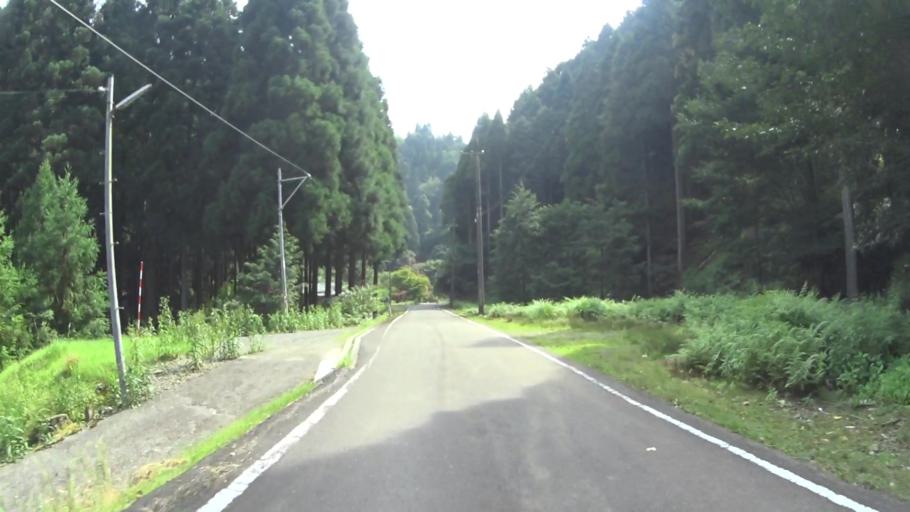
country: JP
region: Fukui
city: Obama
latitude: 35.3442
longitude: 135.6502
